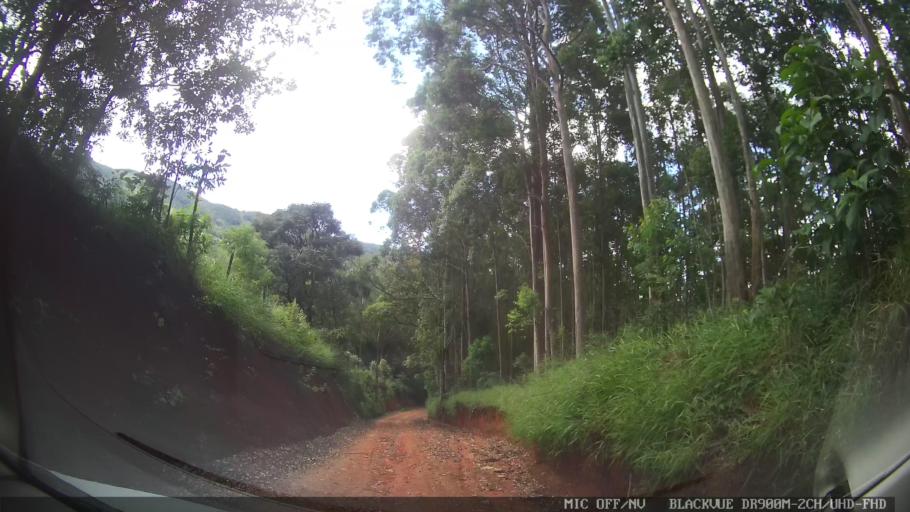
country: BR
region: Minas Gerais
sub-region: Extrema
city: Extrema
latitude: -22.8789
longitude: -46.2932
